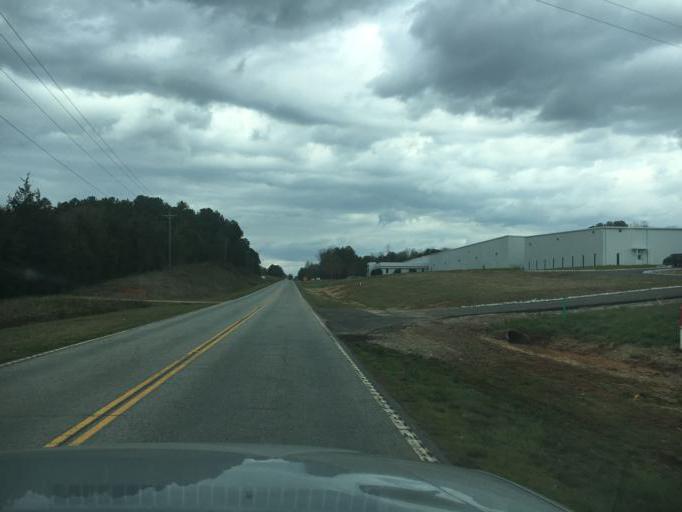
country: US
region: South Carolina
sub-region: Oconee County
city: Walhalla
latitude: 34.7297
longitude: -83.0552
